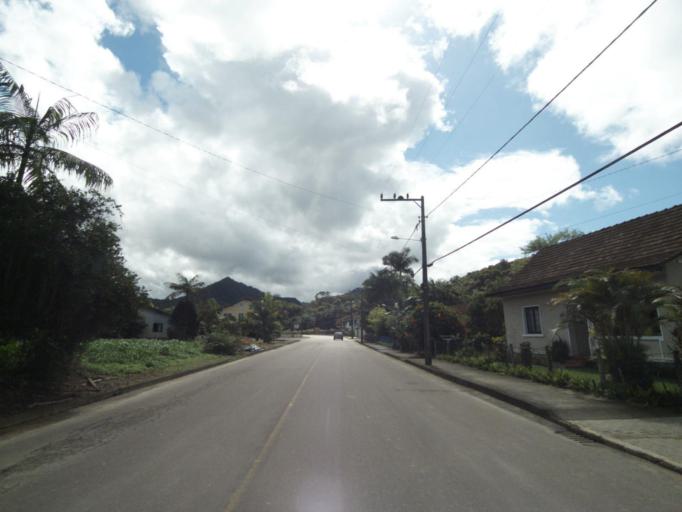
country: BR
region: Santa Catarina
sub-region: Pomerode
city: Pomerode
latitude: -26.6842
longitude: -49.1759
